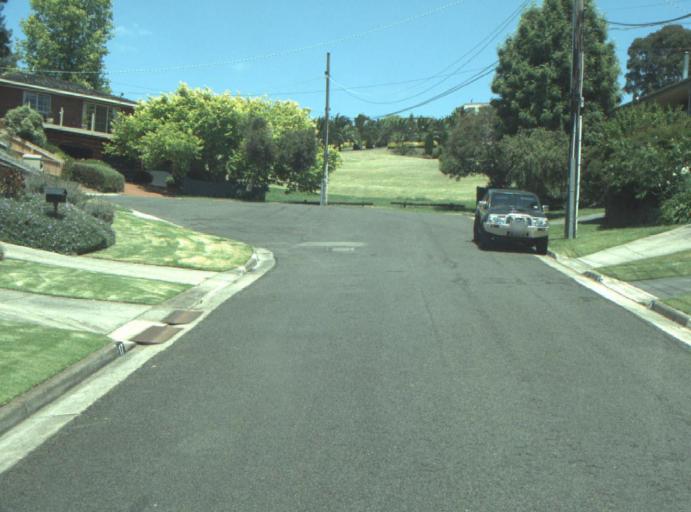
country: AU
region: Victoria
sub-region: Greater Geelong
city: Wandana Heights
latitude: -38.1581
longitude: 144.3169
